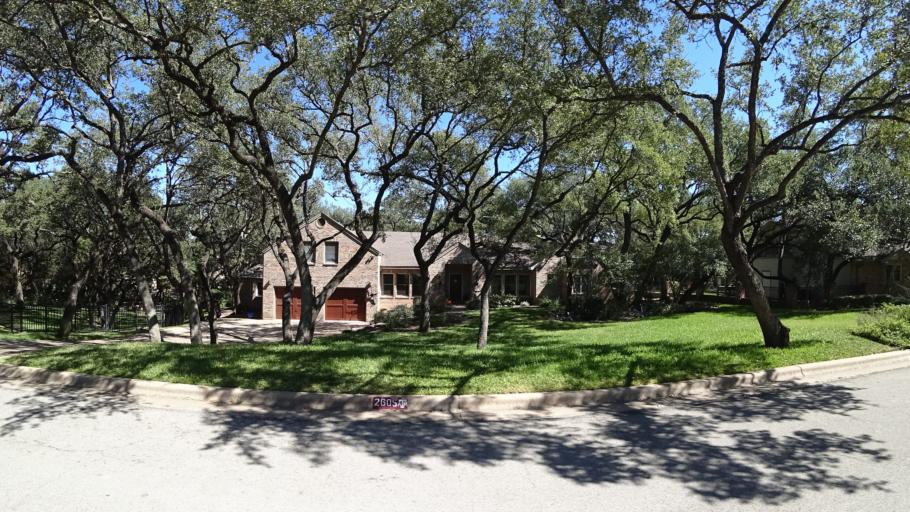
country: US
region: Texas
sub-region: Travis County
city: West Lake Hills
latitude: 30.3133
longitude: -97.7859
